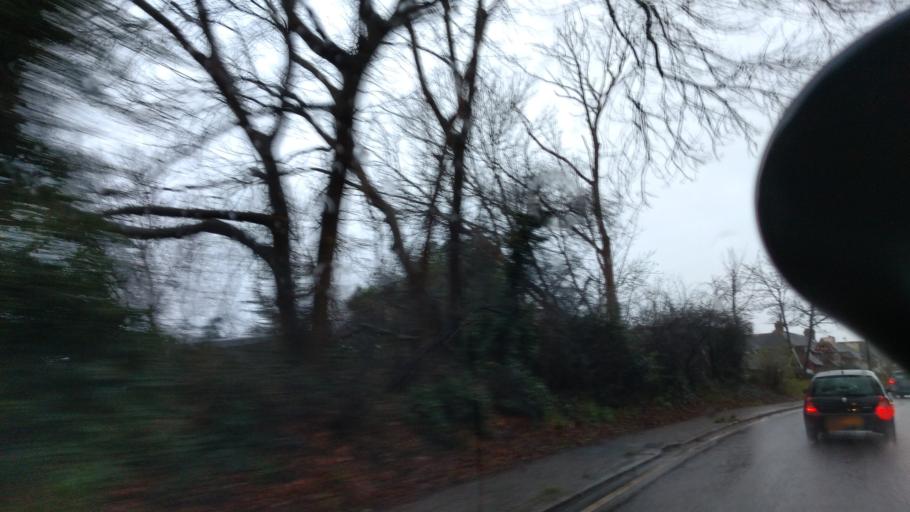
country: GB
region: England
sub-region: West Sussex
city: Broadwater
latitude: 50.8385
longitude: -0.3956
